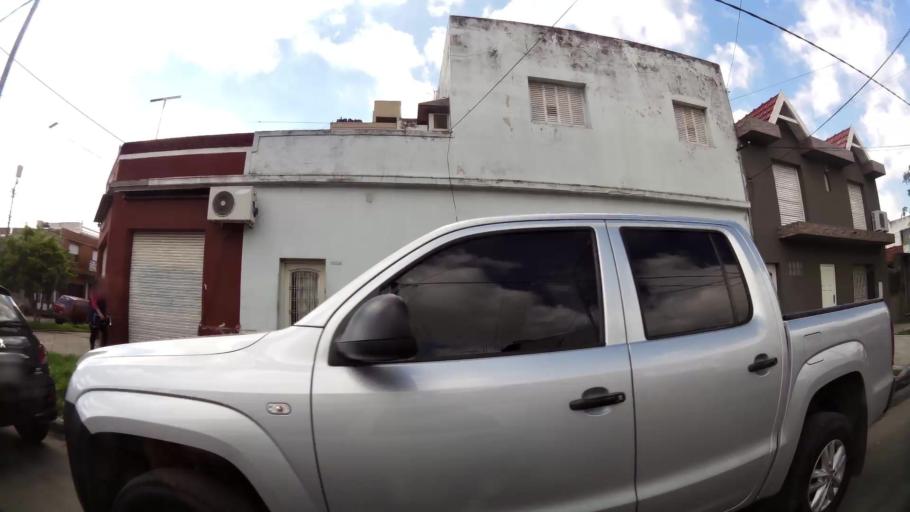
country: AR
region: Buenos Aires
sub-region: Partido de Lanus
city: Lanus
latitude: -34.6881
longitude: -58.4126
